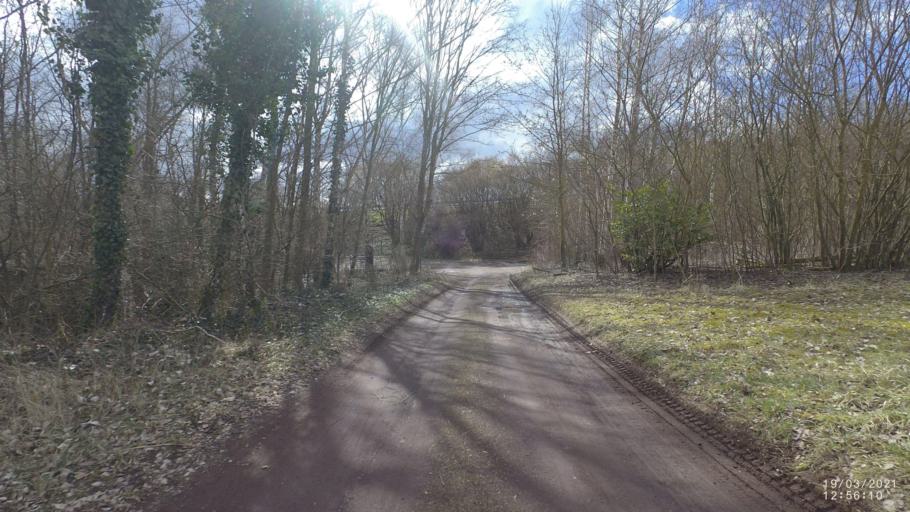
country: DE
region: Rheinland-Pfalz
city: Kretz
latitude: 50.3933
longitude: 7.3518
